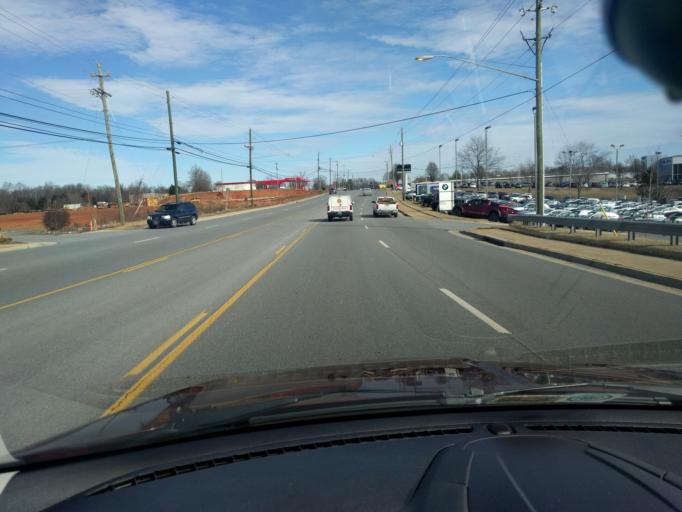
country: US
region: Virginia
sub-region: City of Lynchburg
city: West Lynchburg
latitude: 37.3948
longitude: -79.2322
